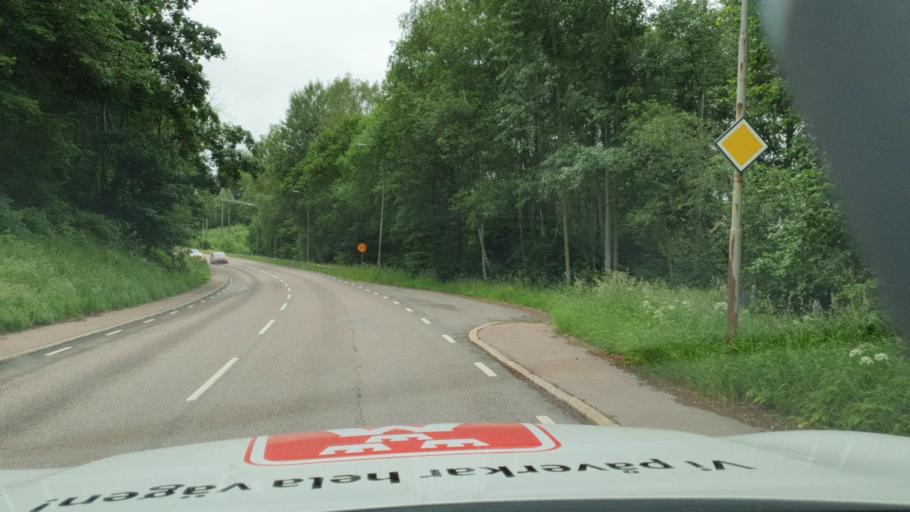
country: SE
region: Vaermland
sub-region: Karlstads Kommun
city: Edsvalla
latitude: 59.4405
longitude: 13.2092
